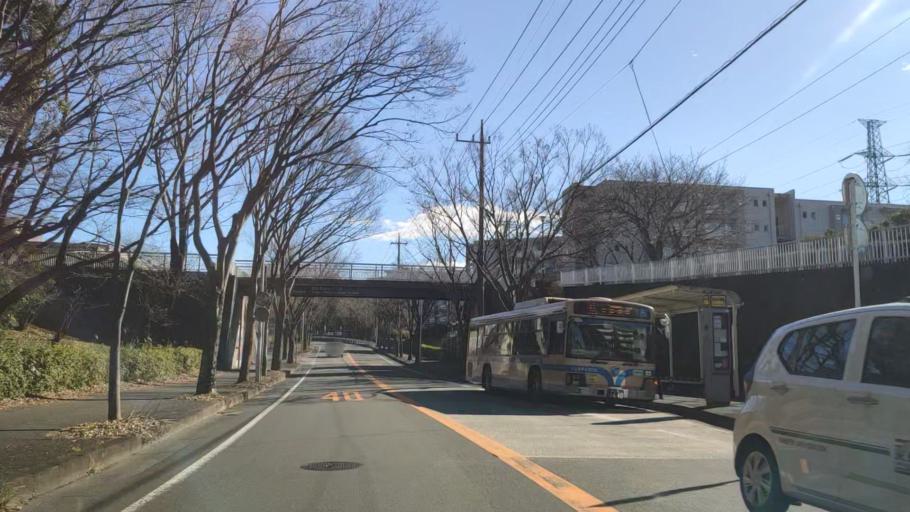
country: JP
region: Tokyo
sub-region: Machida-shi
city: Machida
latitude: 35.5128
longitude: 139.5007
